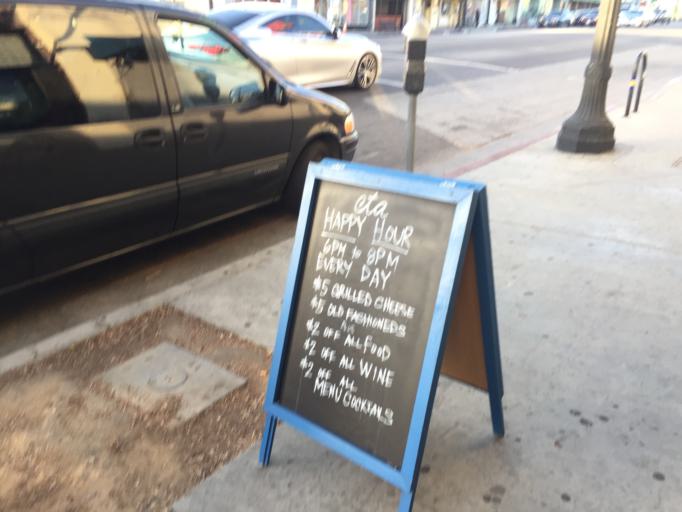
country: US
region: California
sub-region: Los Angeles County
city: South Pasadena
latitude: 34.1094
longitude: -118.1930
